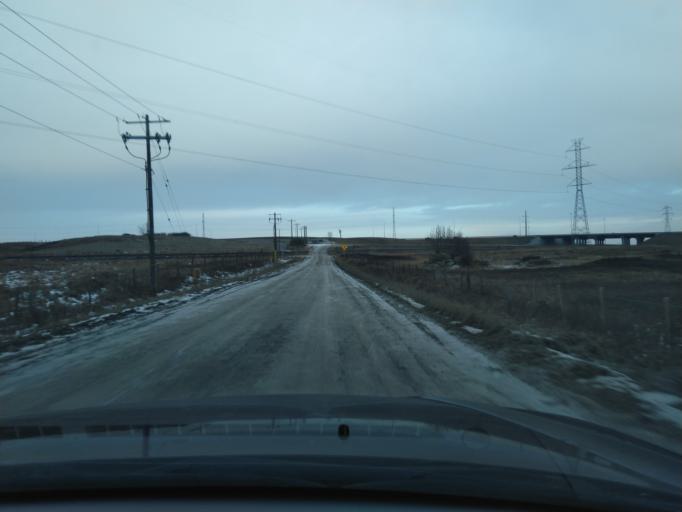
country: CA
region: Alberta
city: Airdrie
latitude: 51.1712
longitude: -114.0249
